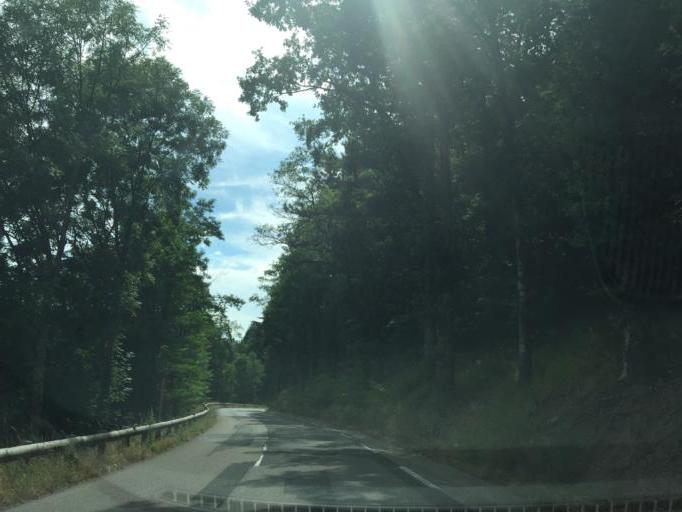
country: FR
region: Rhone-Alpes
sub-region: Departement de la Loire
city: Saint-Etienne
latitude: 45.4104
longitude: 4.4275
